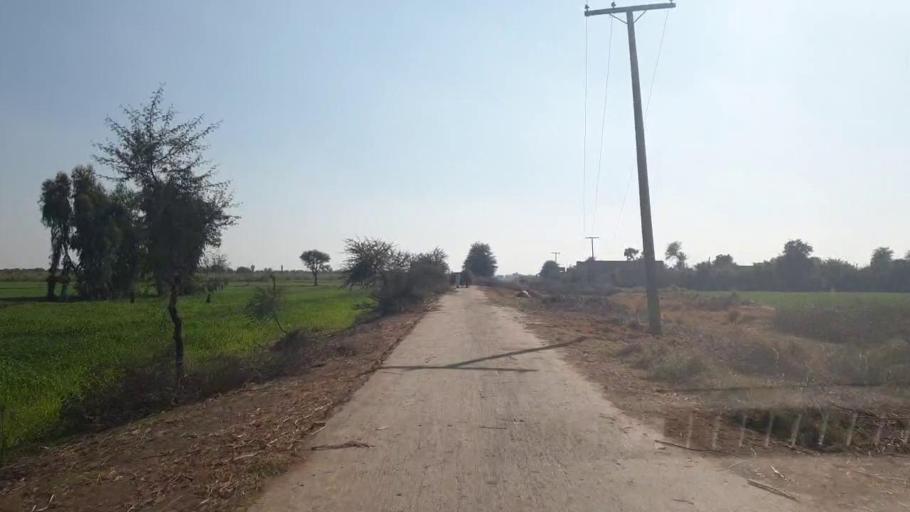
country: PK
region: Sindh
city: Shahdadpur
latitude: 25.9135
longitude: 68.5567
